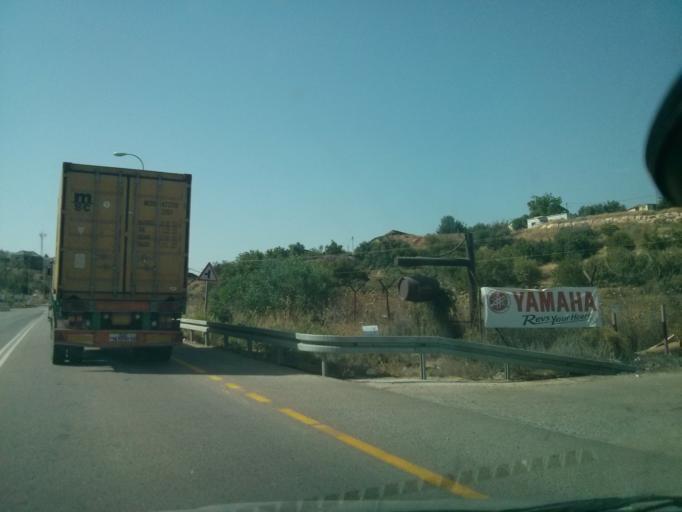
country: IL
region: Jerusalem
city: Bet Shemesh
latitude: 31.6766
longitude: 35.0054
